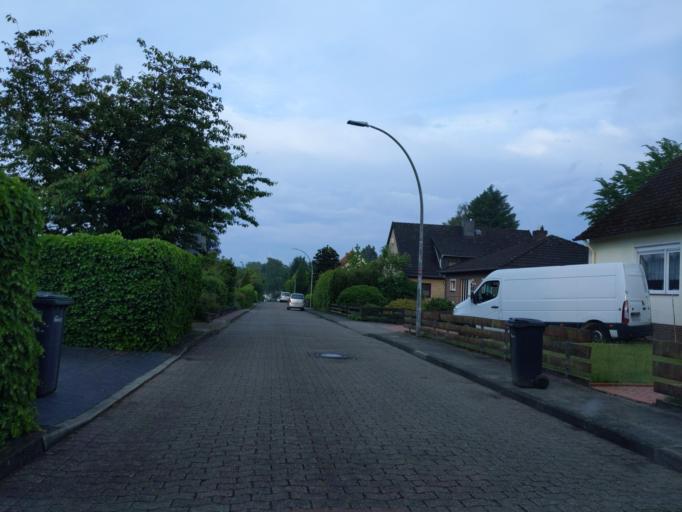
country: DE
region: Lower Saxony
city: Walsrode
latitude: 52.8708
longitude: 9.5900
